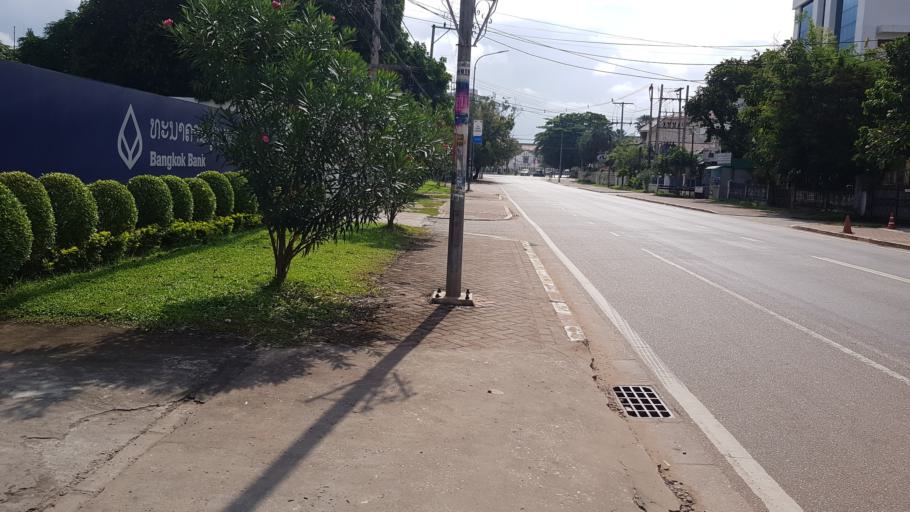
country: LA
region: Vientiane
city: Vientiane
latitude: 17.9651
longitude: 102.6108
